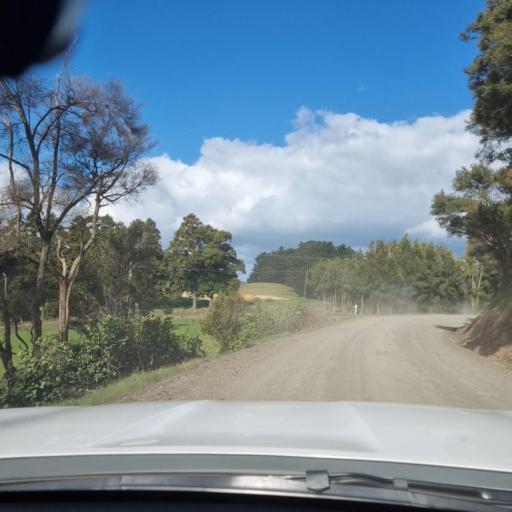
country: NZ
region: Auckland
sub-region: Auckland
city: Wellsford
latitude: -36.3150
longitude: 174.1341
